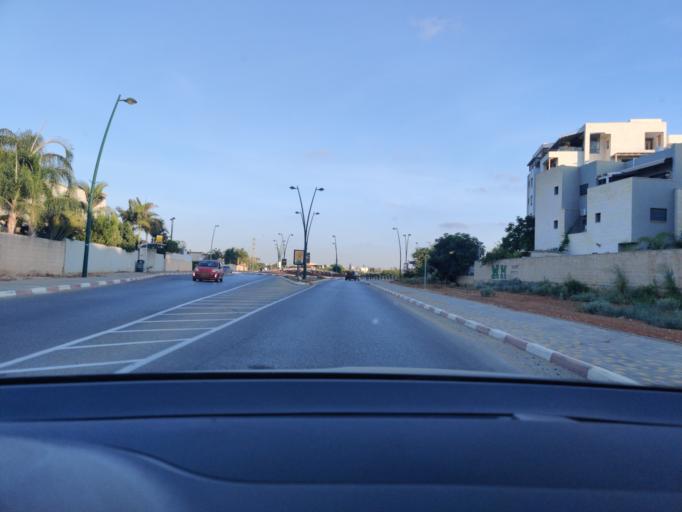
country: IL
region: Central District
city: Elyakhin
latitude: 32.4281
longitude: 34.9409
